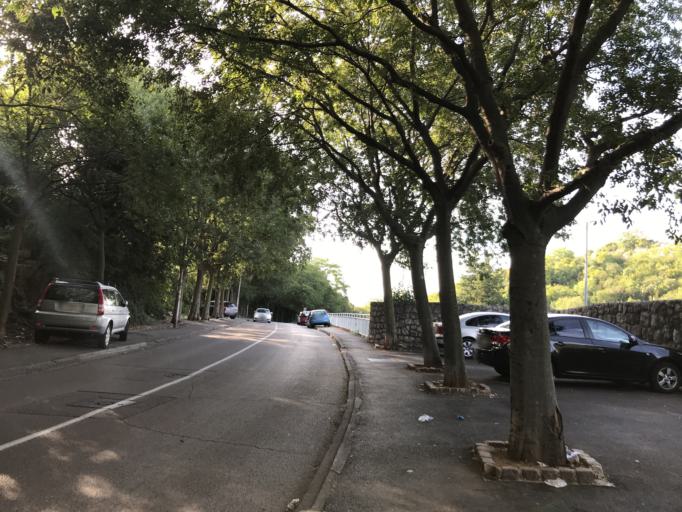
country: HR
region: Primorsko-Goranska
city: Drenova
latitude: 45.3355
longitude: 14.4401
